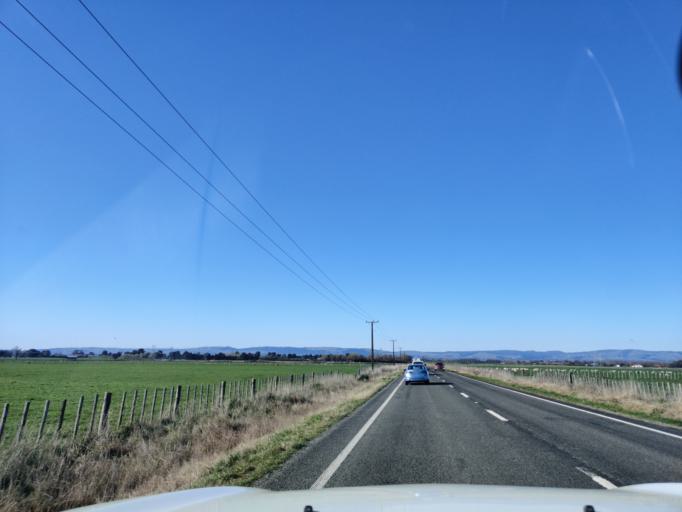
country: NZ
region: Manawatu-Wanganui
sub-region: Palmerston North City
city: Palmerston North
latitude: -40.2859
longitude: 175.5625
